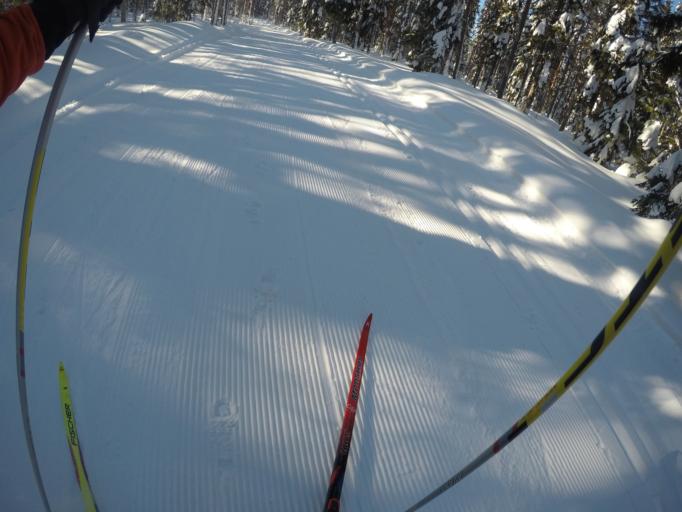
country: SE
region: Vaesternorrland
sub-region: Sundsvalls Kommun
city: Sundsvall
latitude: 62.3688
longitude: 17.2979
